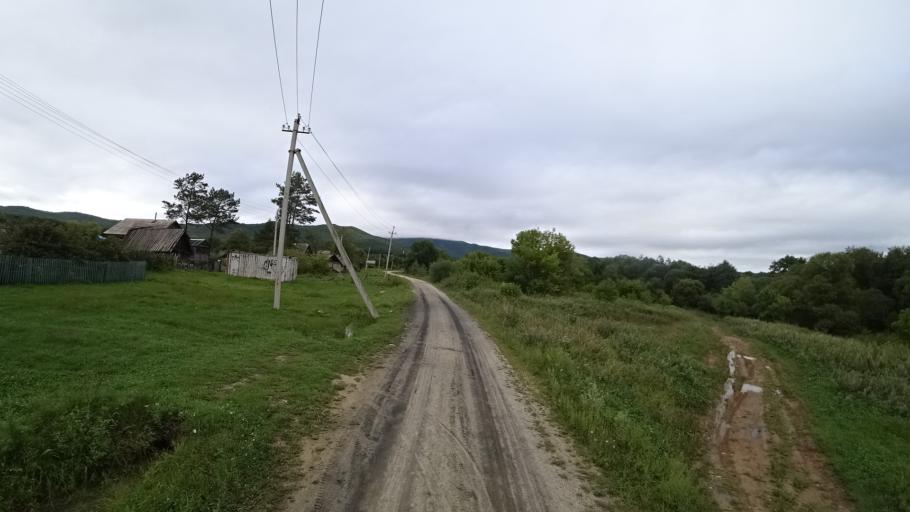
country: RU
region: Primorskiy
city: Rettikhovka
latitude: 44.1387
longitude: 132.6425
